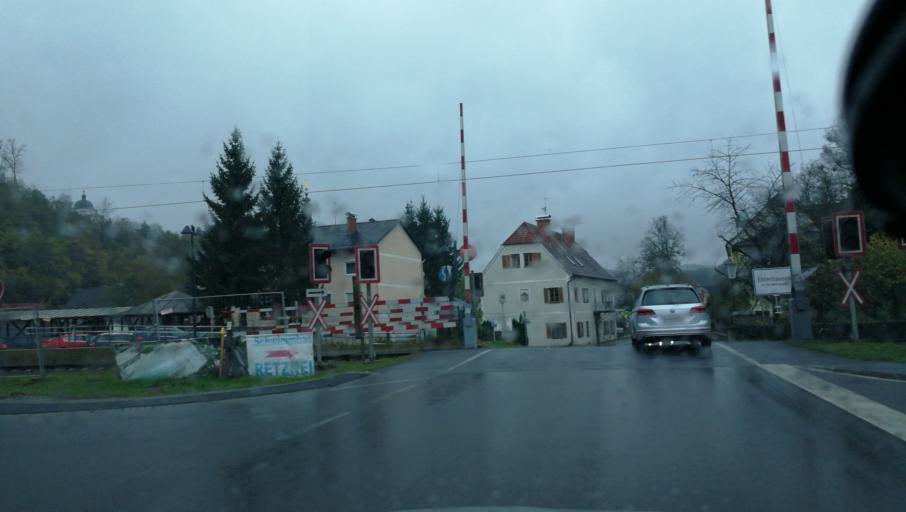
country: AT
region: Styria
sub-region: Politischer Bezirk Leibnitz
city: Ehrenhausen
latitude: 46.7280
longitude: 15.5846
